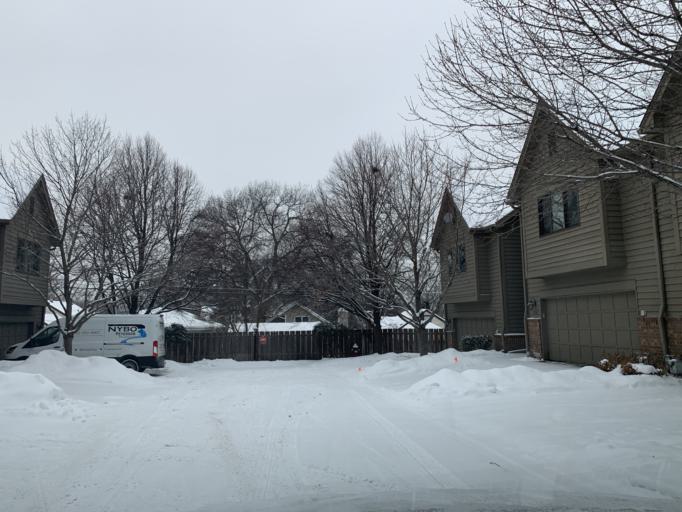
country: US
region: Minnesota
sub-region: Hennepin County
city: Saint Louis Park
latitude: 44.9499
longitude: -93.3380
